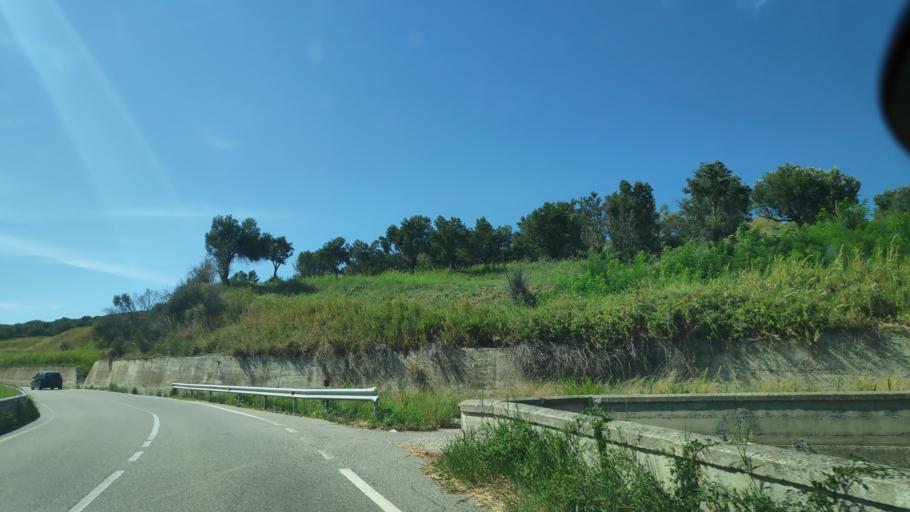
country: IT
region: Calabria
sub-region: Provincia di Catanzaro
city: Staletti
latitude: 38.7845
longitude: 16.5464
